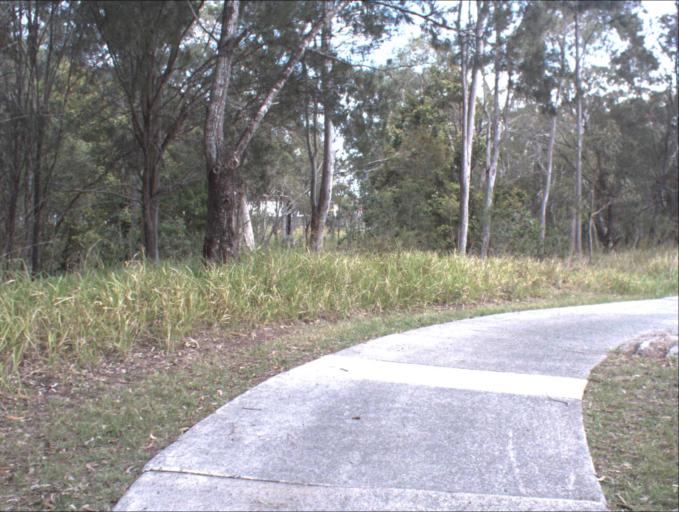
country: AU
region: Queensland
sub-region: Logan
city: Park Ridge South
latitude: -27.6737
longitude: 153.0547
